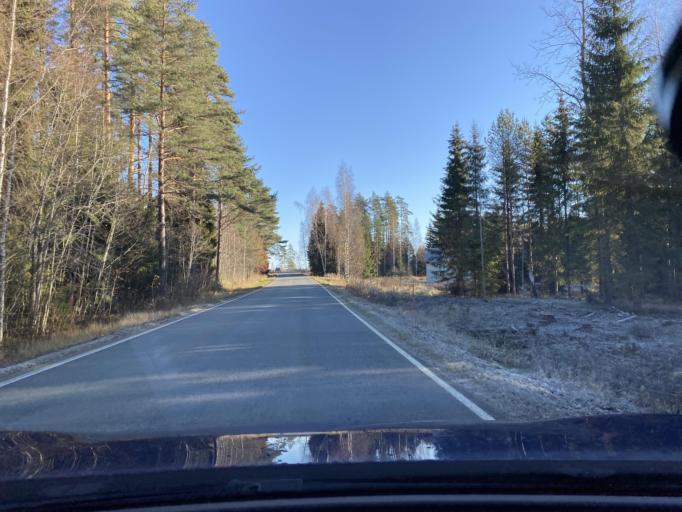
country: FI
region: Pirkanmaa
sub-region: Etelae-Pirkanmaa
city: Akaa
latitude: 61.0109
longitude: 23.8990
